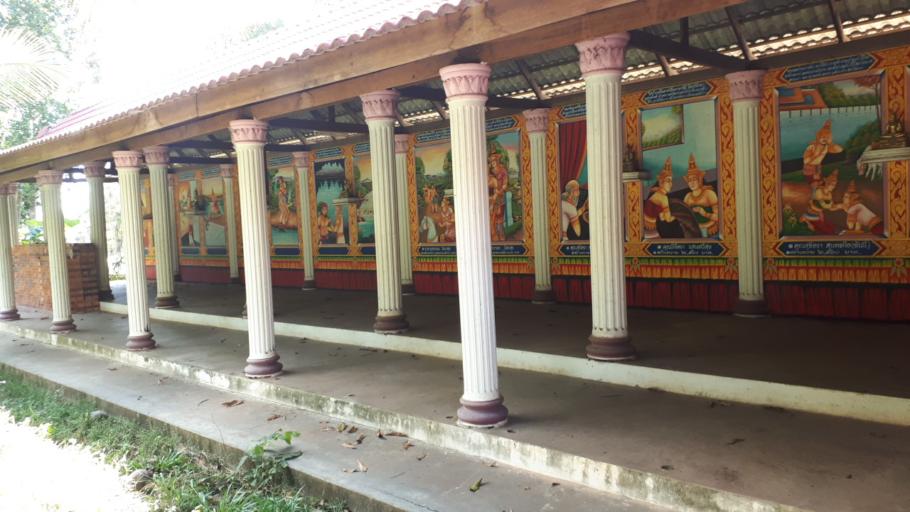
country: TH
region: Changwat Ubon Ratchathani
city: Warin Chamrap
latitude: 15.1342
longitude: 104.8449
